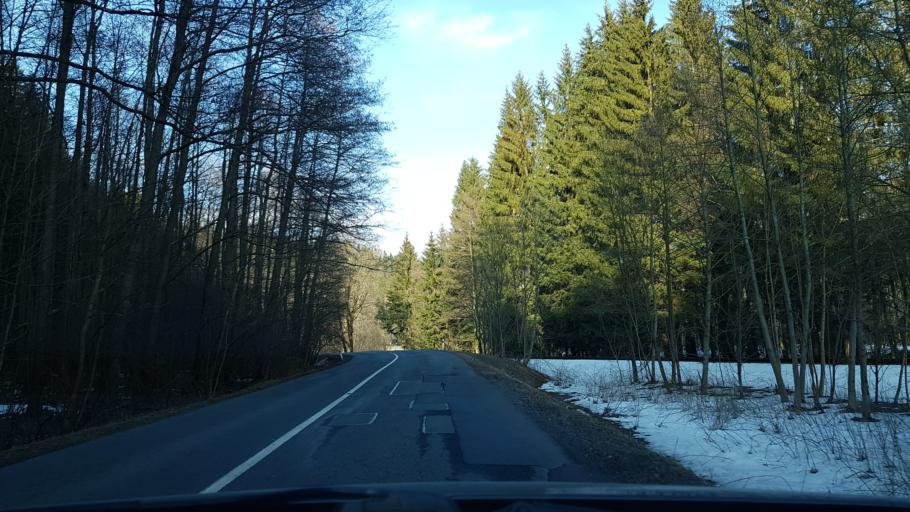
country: CZ
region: Olomoucky
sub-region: Okres Sumperk
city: Hanusovice
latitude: 50.0849
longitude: 16.9694
